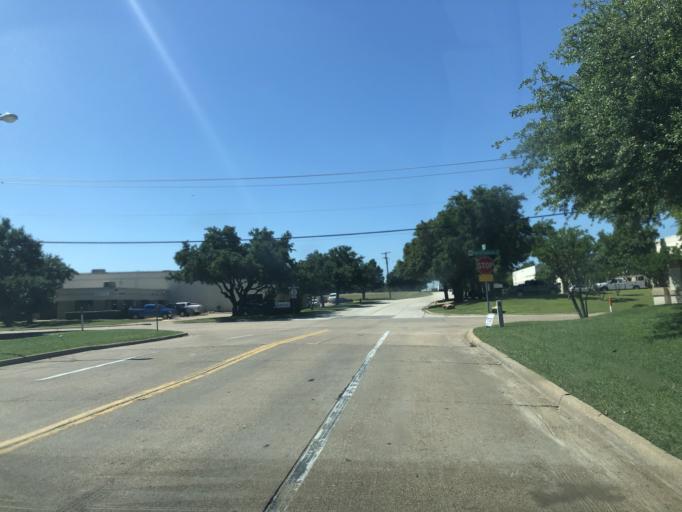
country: US
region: Texas
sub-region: Tarrant County
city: Euless
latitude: 32.7939
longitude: -97.0419
